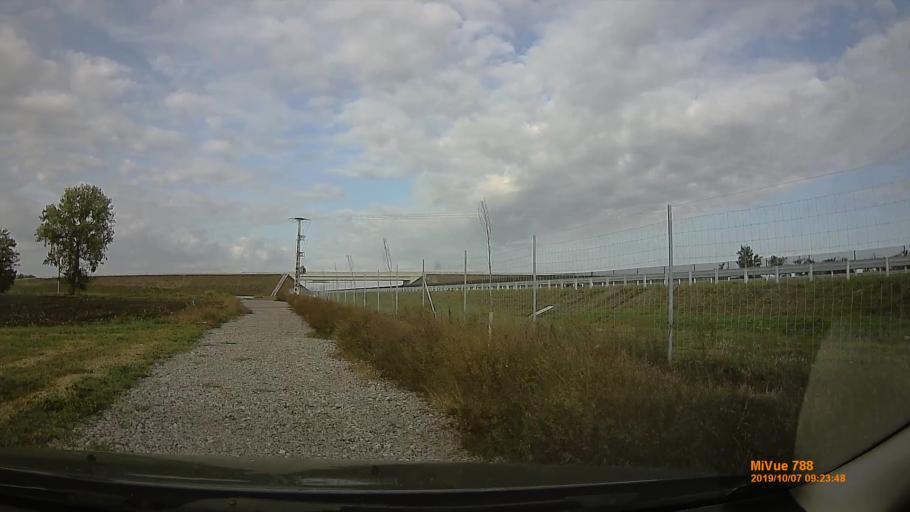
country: HU
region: Bekes
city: Szarvas
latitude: 46.8135
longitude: 20.6525
